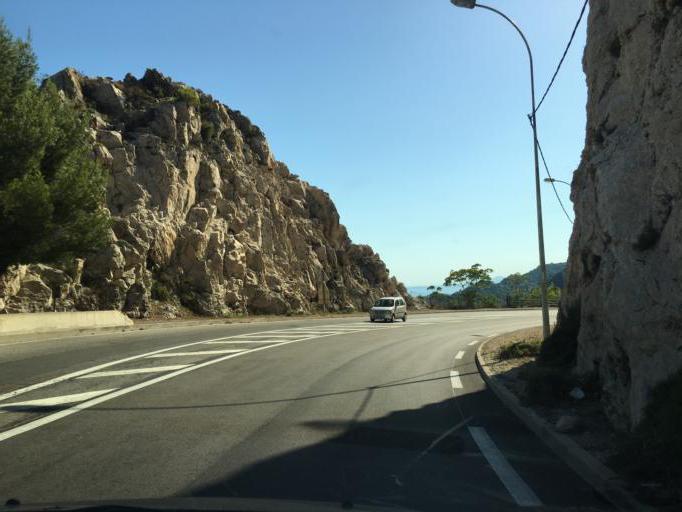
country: FR
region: Provence-Alpes-Cote d'Azur
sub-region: Departement des Alpes-Maritimes
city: Eze
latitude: 43.7283
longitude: 7.3569
